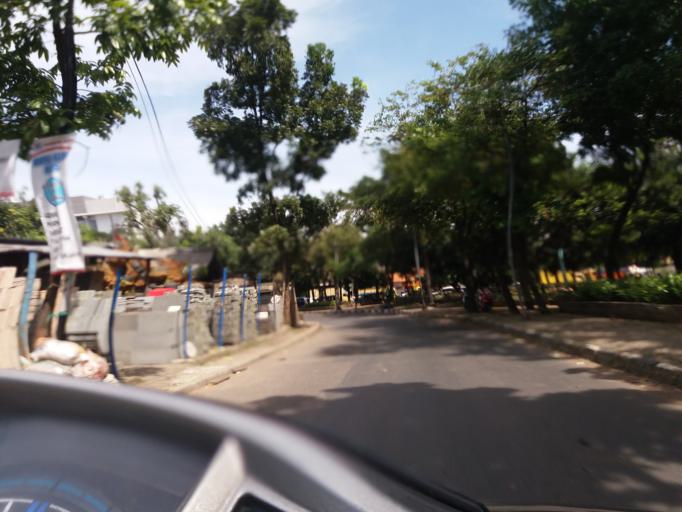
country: ID
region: West Java
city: Bandung
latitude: -6.9479
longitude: 107.6344
